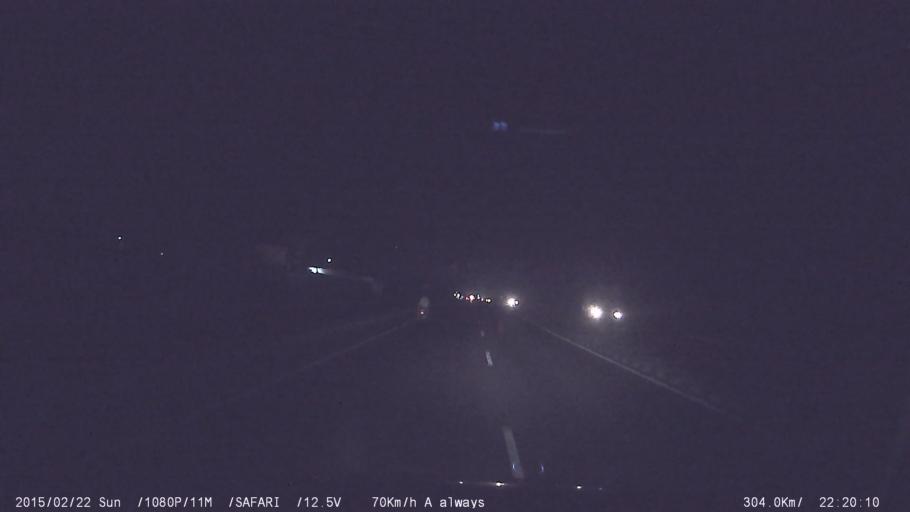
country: IN
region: Tamil Nadu
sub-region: Karur
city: Karur
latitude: 10.9882
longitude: 78.0654
